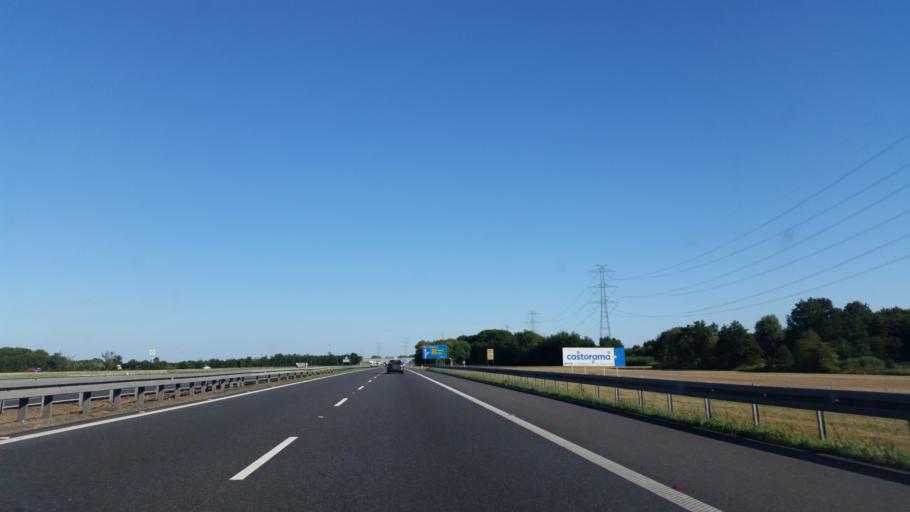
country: PL
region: Opole Voivodeship
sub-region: Powiat brzeski
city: Skarbimierz Osiedle
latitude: 50.7886
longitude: 17.3368
